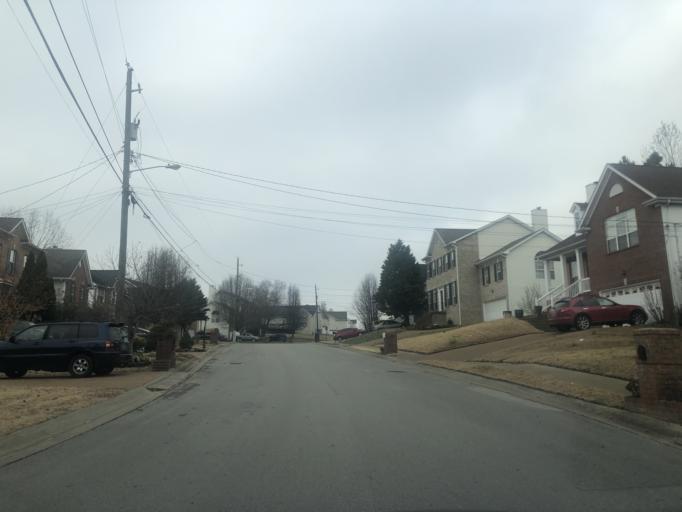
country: US
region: Tennessee
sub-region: Rutherford County
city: La Vergne
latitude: 36.0673
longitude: -86.6478
